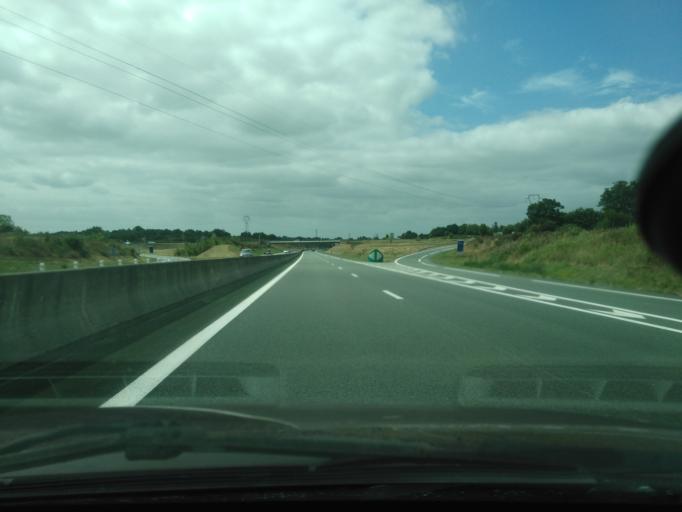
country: FR
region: Pays de la Loire
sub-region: Departement de la Vendee
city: La Roche-sur-Yon
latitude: 46.6407
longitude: -1.3961
